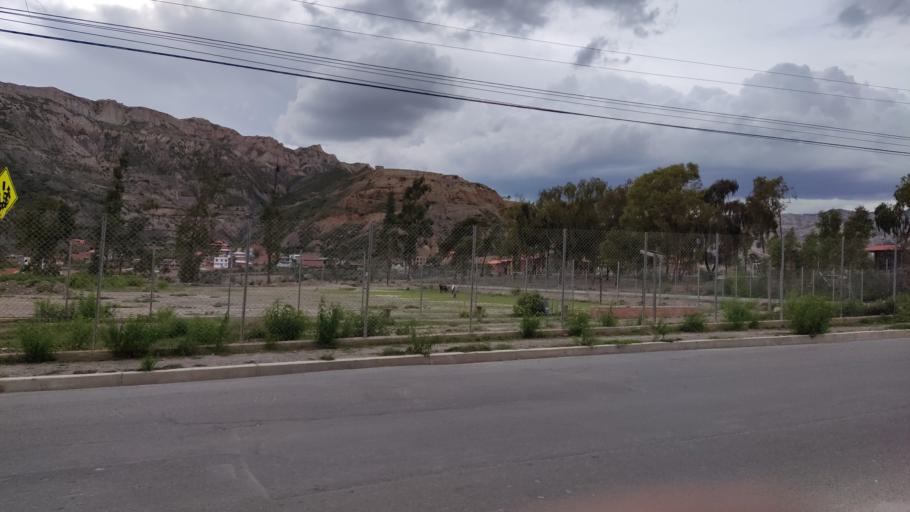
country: BO
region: La Paz
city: La Paz
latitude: -16.5794
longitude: -68.0804
